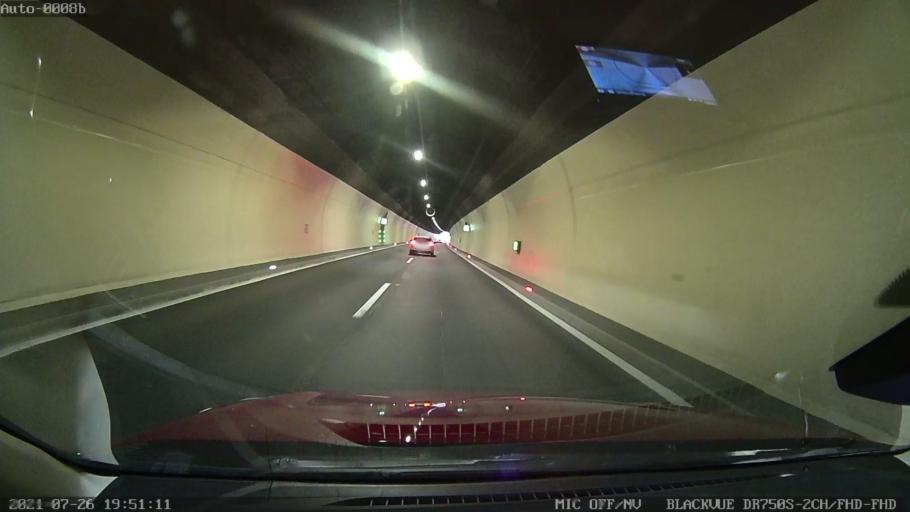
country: AT
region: Styria
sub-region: Politischer Bezirk Liezen
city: Selzthal
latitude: 47.5422
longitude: 14.3038
